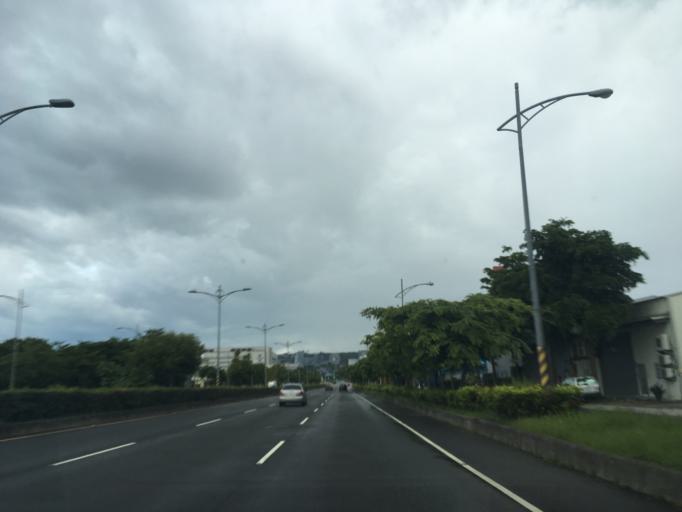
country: TW
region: Taiwan
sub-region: Taichung City
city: Taichung
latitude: 24.2049
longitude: 120.6330
